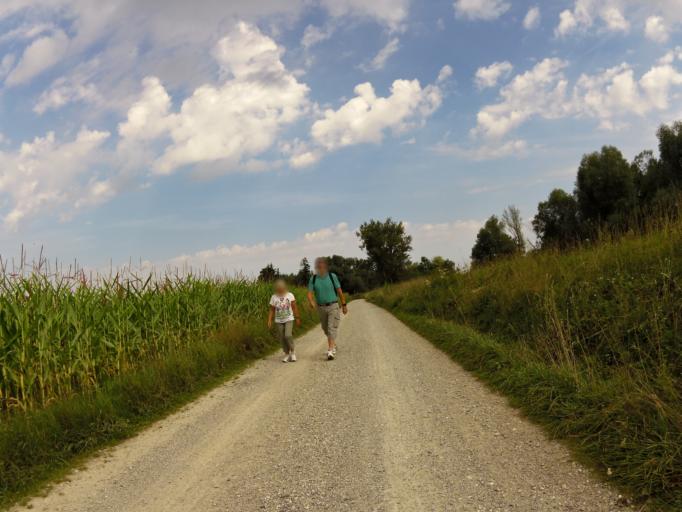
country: DE
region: Bavaria
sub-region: Upper Bavaria
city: Pahl
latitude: 47.9255
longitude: 11.1451
